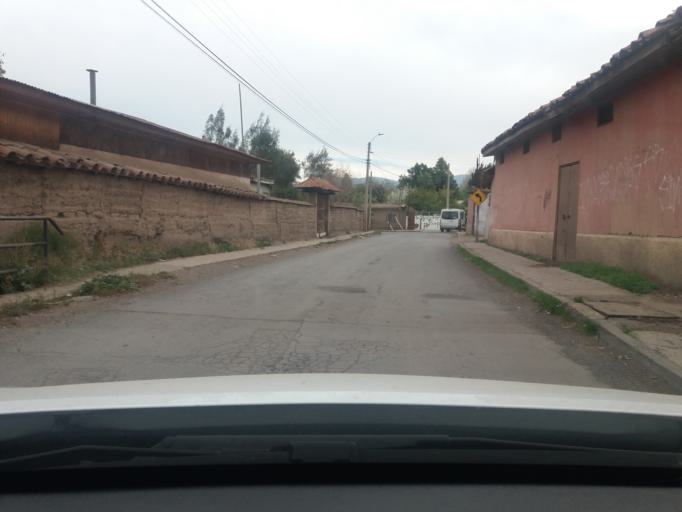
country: CL
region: Valparaiso
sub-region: Provincia de Los Andes
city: Los Andes
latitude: -32.8433
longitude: -70.6300
